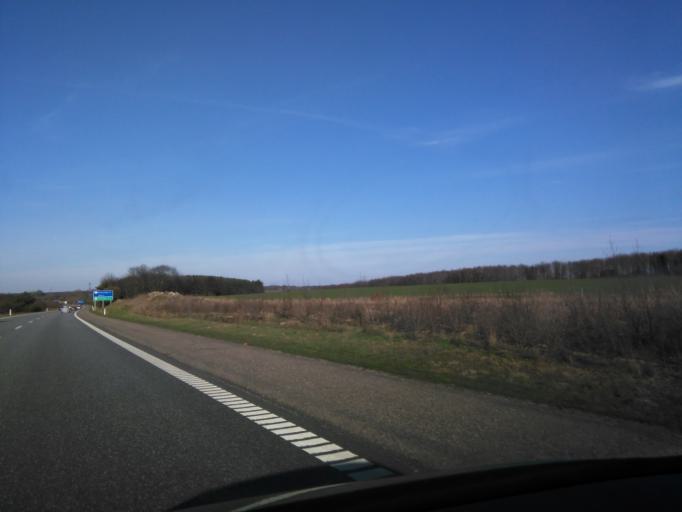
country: DK
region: Central Jutland
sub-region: Skanderborg Kommune
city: Horning
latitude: 56.0987
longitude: 10.0315
